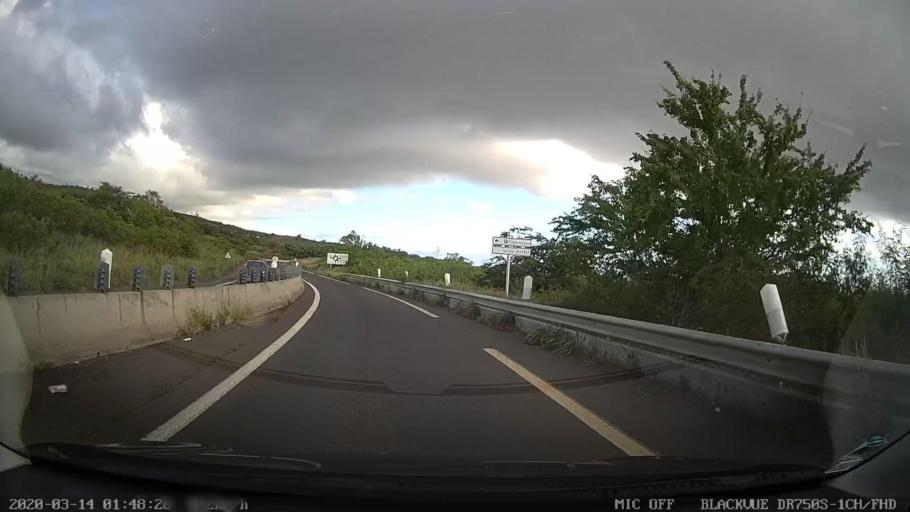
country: RE
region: Reunion
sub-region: Reunion
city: Saint-Paul
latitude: -21.0652
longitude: 55.2469
